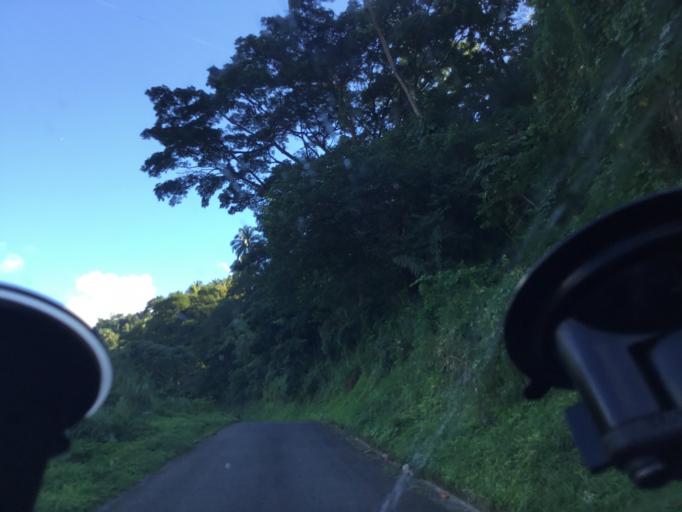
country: VC
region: Saint David
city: Chateaubelair
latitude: 13.2975
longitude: -61.2283
